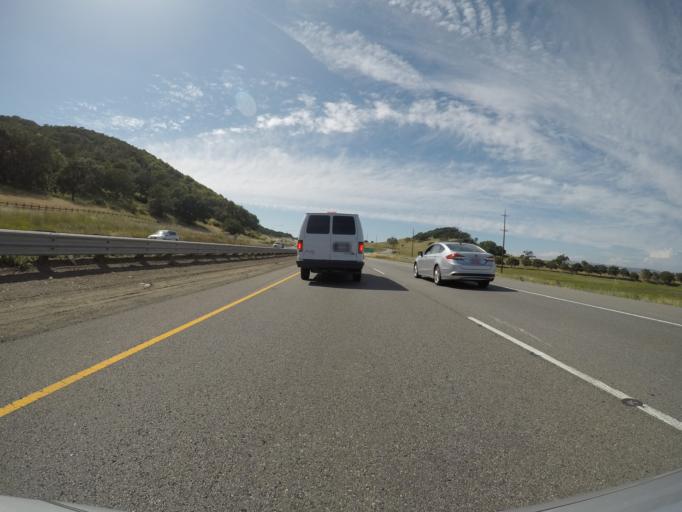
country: US
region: California
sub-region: Marin County
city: Novato
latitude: 38.1600
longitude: -122.5711
